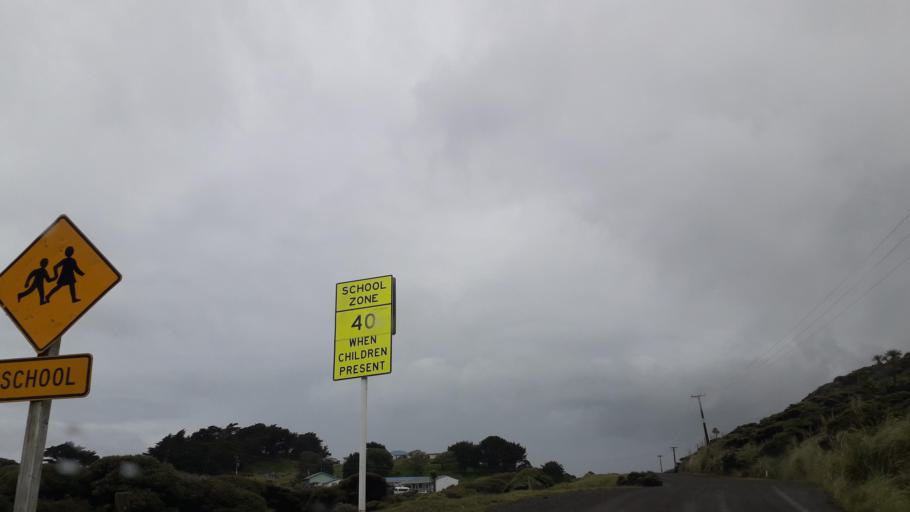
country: NZ
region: Northland
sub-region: Far North District
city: Ahipara
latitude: -35.4378
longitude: 173.2864
